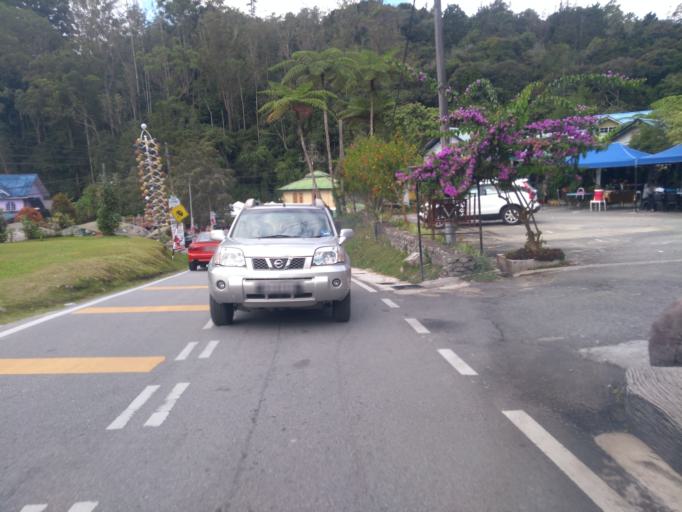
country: MY
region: Pahang
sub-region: Cameron Highlands
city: Tanah Rata
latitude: 4.4776
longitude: 101.3814
